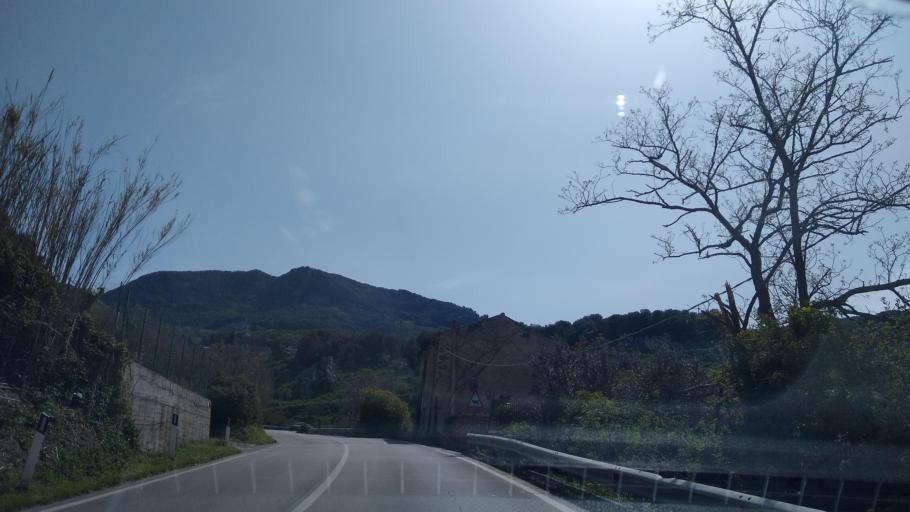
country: IT
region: Sicily
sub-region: Palermo
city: Giacalone
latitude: 38.0374
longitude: 13.2192
